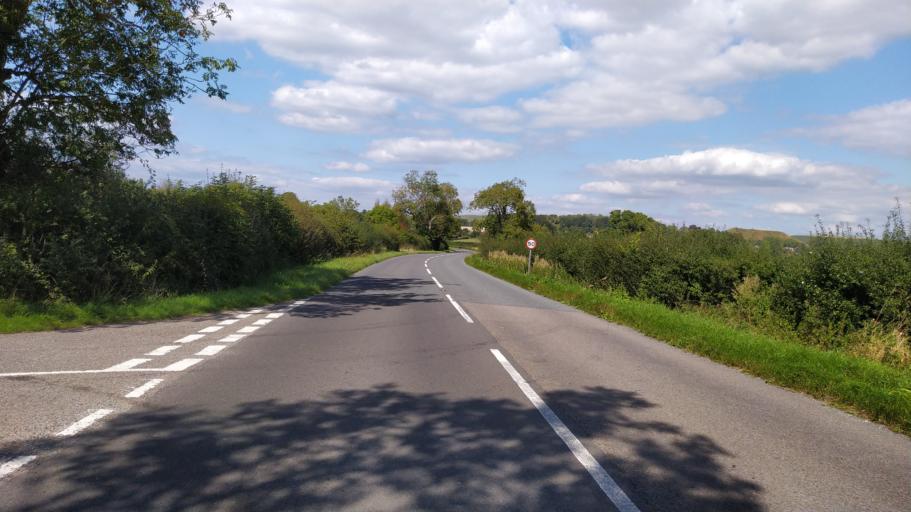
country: GB
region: England
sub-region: Wiltshire
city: Mere
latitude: 51.0795
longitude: -2.2807
